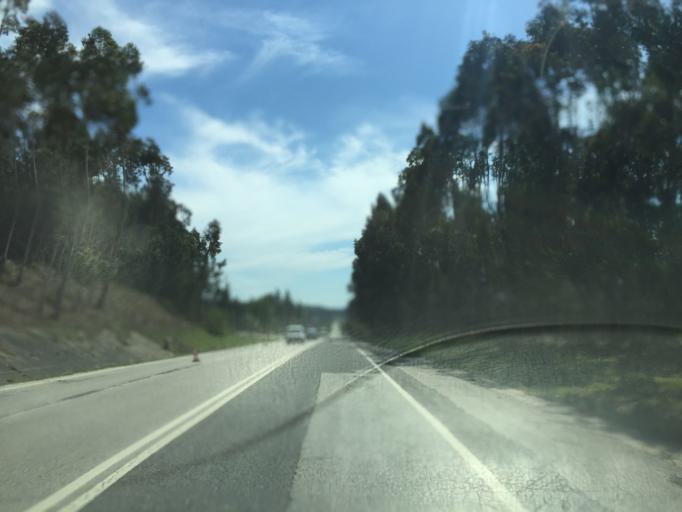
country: PT
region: Coimbra
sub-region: Soure
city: Soure
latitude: 39.9896
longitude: -8.6107
